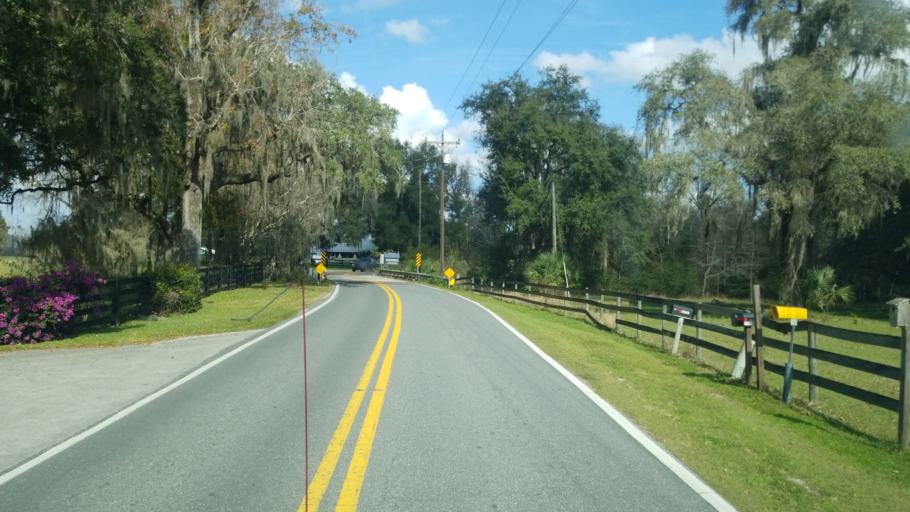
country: US
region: Florida
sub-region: Citrus County
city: Floral City
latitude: 28.7464
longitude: -82.2634
